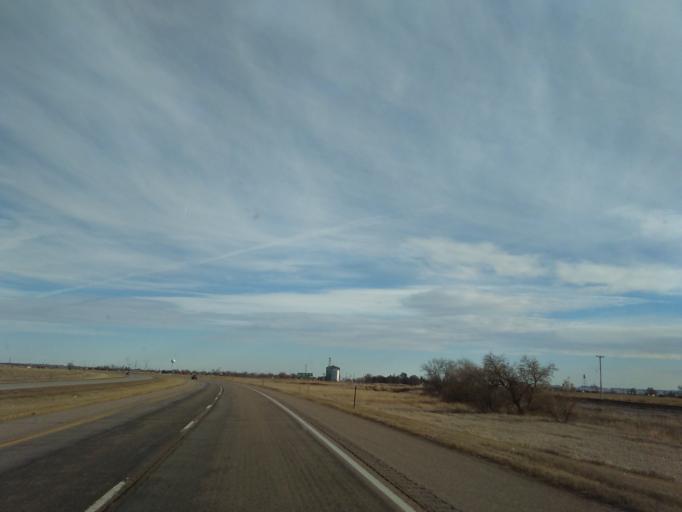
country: US
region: Nebraska
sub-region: Scotts Bluff County
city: Gering
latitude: 41.8162
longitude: -103.5285
